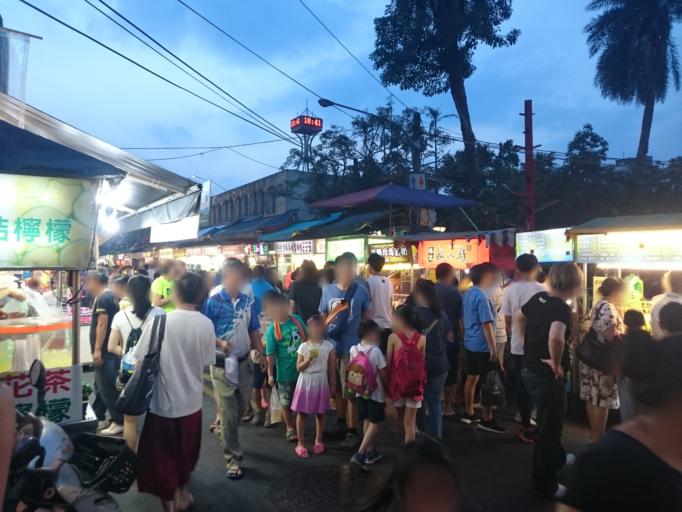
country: TW
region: Taiwan
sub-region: Yilan
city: Yilan
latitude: 24.6756
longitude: 121.7690
